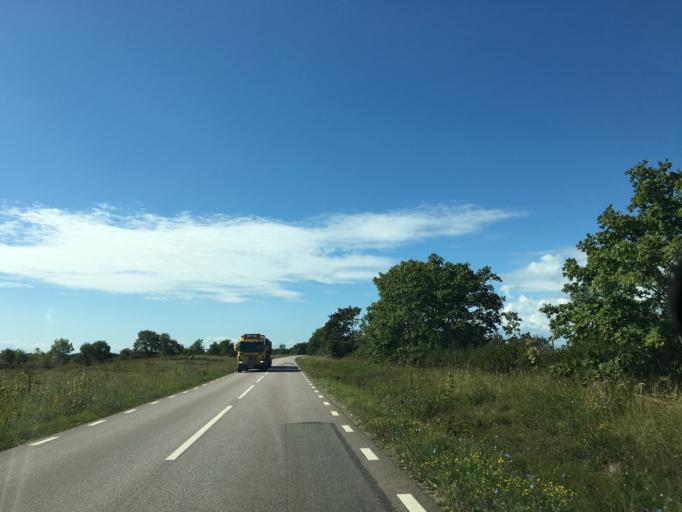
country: SE
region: Kalmar
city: Faerjestaden
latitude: 56.5671
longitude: 16.4542
